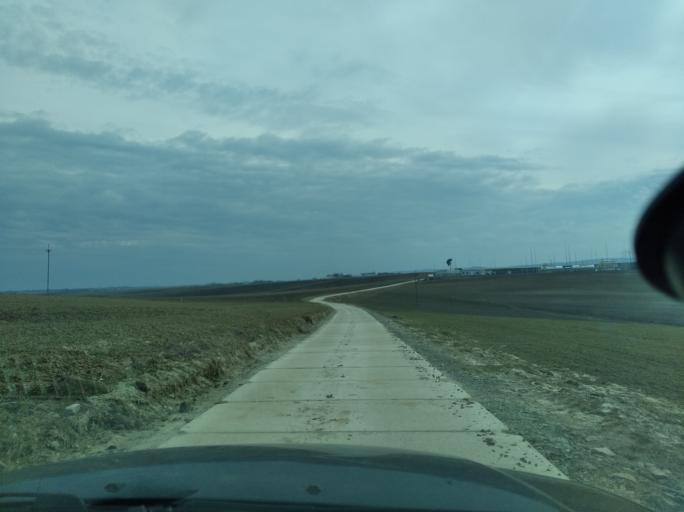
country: PL
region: Subcarpathian Voivodeship
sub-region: Powiat jaroslawski
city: Rokietnica
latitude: 49.9282
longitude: 22.5939
